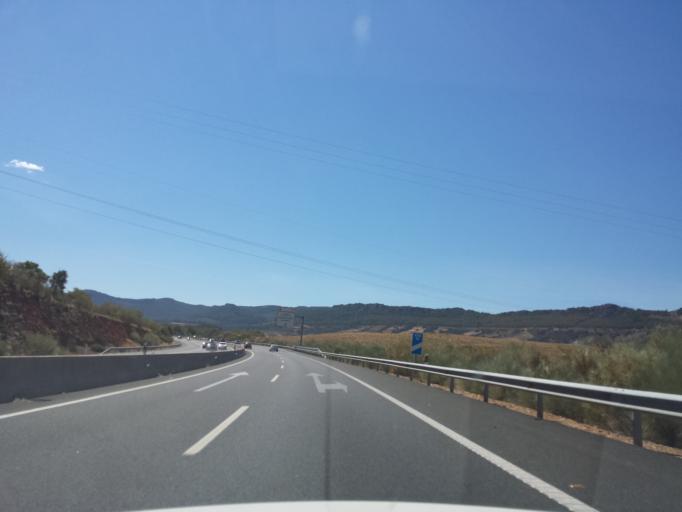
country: ES
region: Extremadura
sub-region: Provincia de Caceres
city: Casas de Miravete
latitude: 39.7361
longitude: -5.7236
